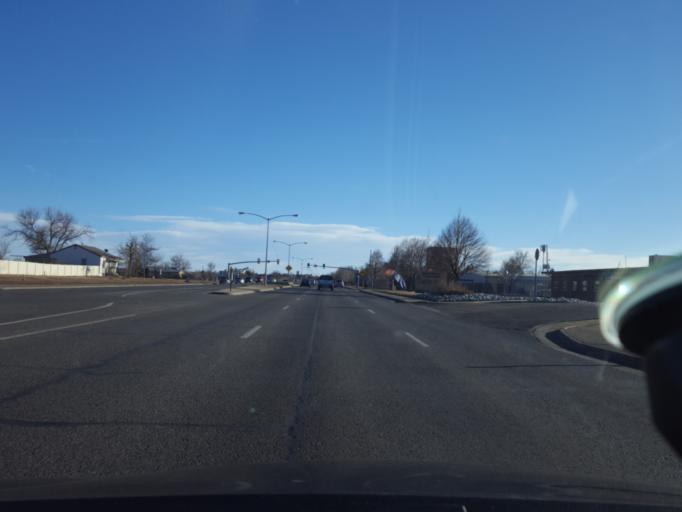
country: US
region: Colorado
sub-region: Adams County
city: Aurora
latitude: 39.7387
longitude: -104.7913
